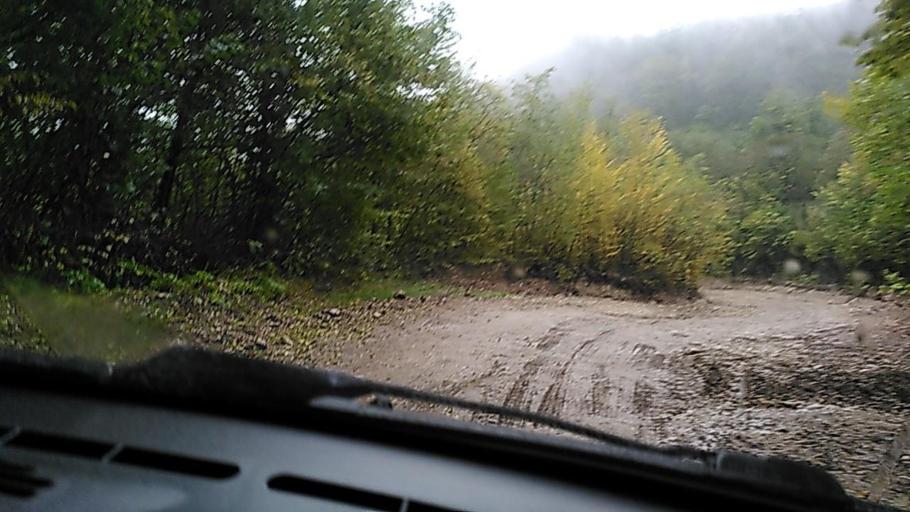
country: RU
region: Kabardino-Balkariya
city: Belaya Rechka
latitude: 43.3825
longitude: 43.4359
